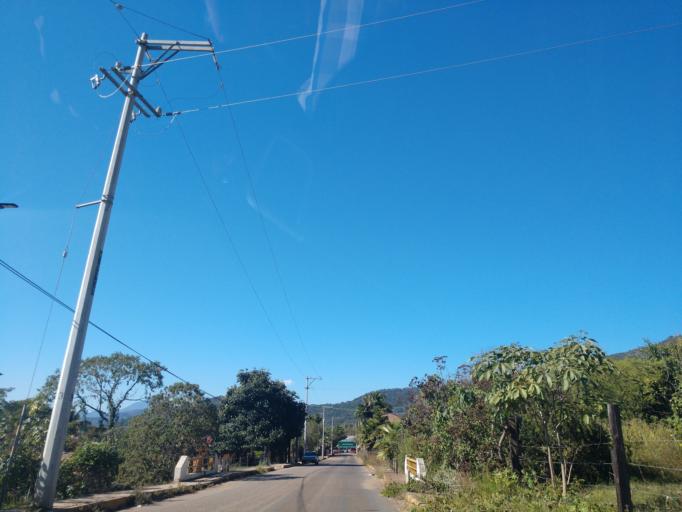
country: MX
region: Nayarit
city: Compostela
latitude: 21.2820
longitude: -104.8768
